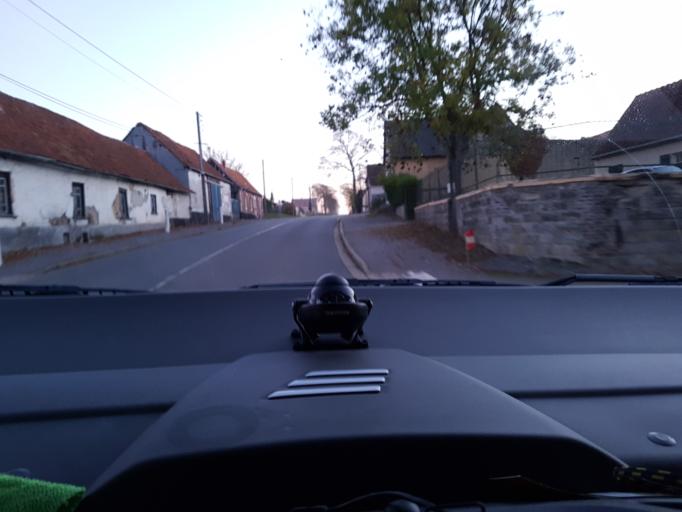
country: FR
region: Picardie
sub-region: Departement de la Somme
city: Rue
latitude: 50.2691
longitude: 1.7441
